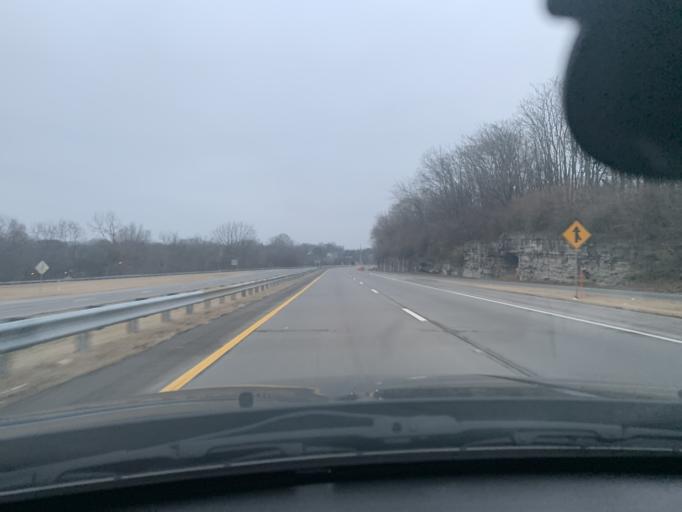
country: US
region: Tennessee
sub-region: Davidson County
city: Nashville
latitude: 36.1928
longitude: -86.7530
